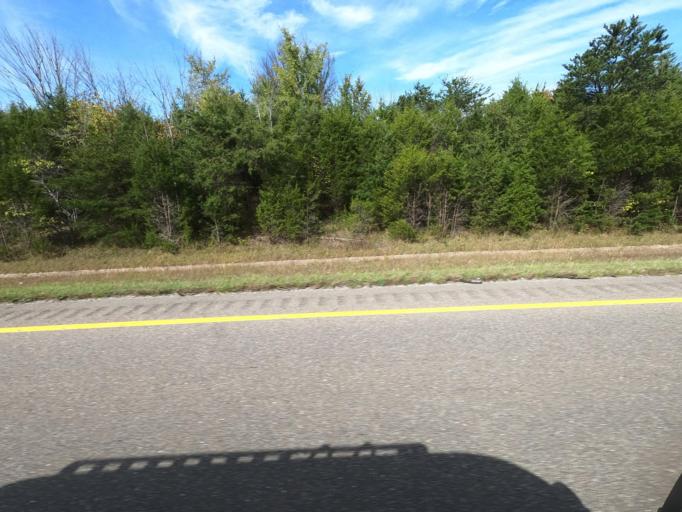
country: US
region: Tennessee
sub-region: Greene County
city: Mosheim
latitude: 36.2430
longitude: -82.9861
